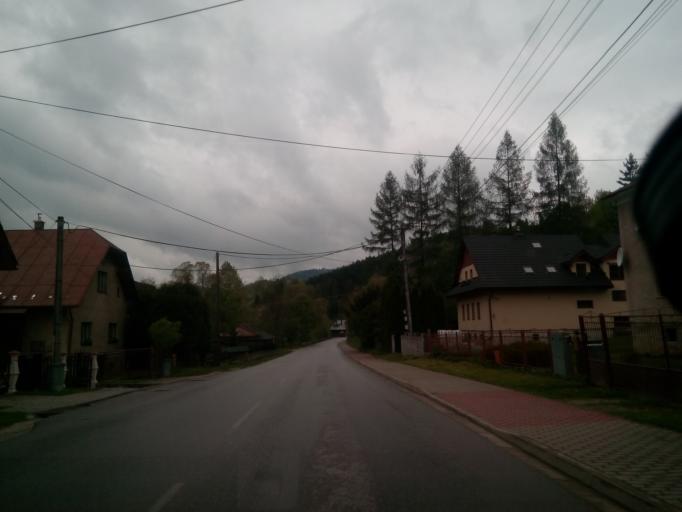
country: SK
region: Zilinsky
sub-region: Okres Zilina
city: Terchova
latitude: 49.2586
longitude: 19.0636
